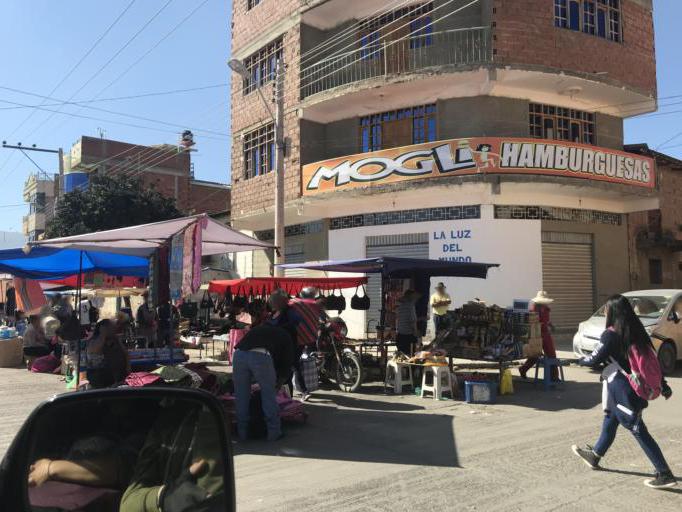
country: BO
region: Cochabamba
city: Punata
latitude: -17.5475
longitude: -65.8408
